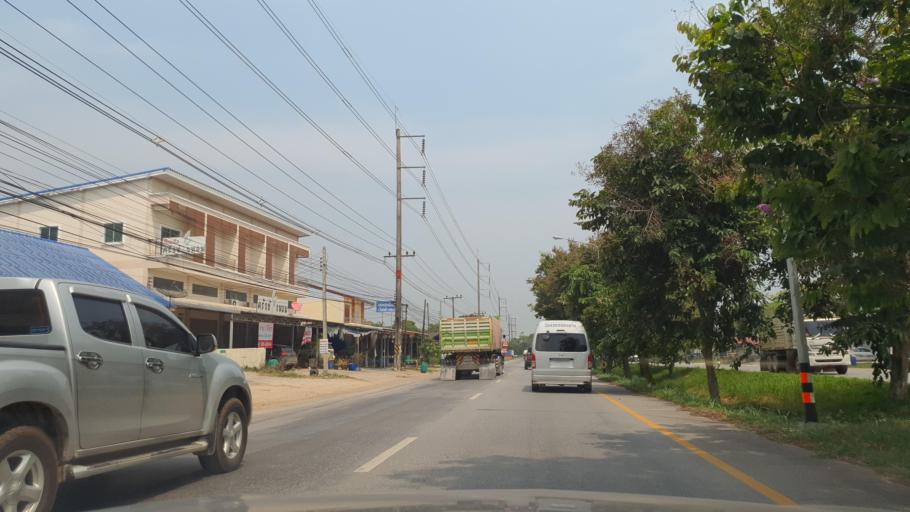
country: TH
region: Rayong
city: Rayong
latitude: 12.6412
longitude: 101.3598
